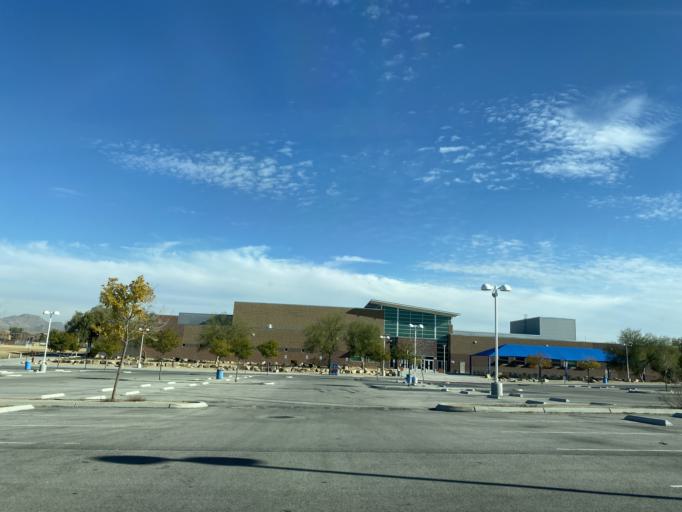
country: US
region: Nevada
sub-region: Clark County
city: North Las Vegas
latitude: 36.2849
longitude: -115.1440
